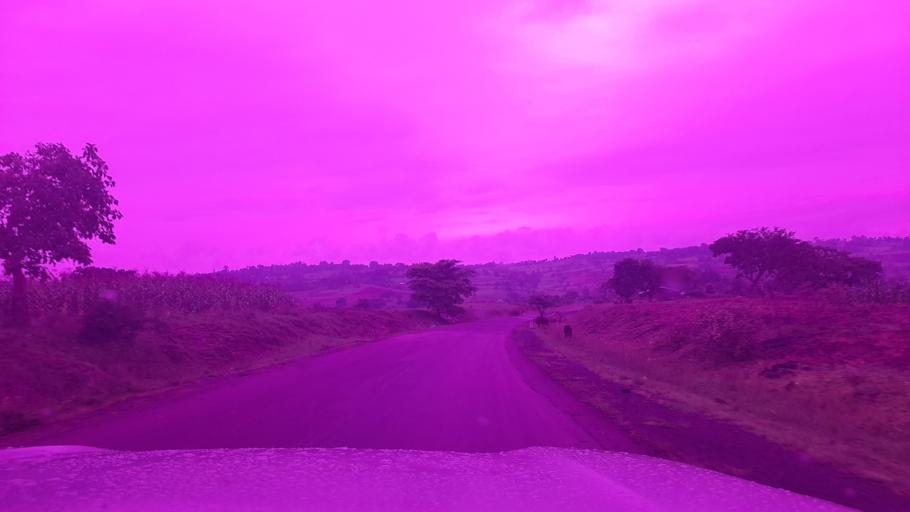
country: ET
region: Oromiya
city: Jima
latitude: 7.7314
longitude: 37.2843
